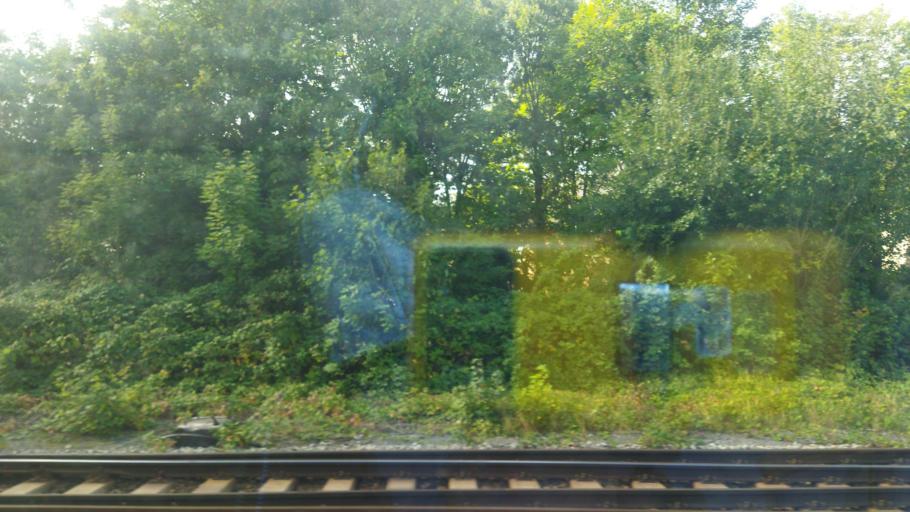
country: DE
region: Lower Saxony
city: Emden
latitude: 53.3651
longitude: 7.1959
